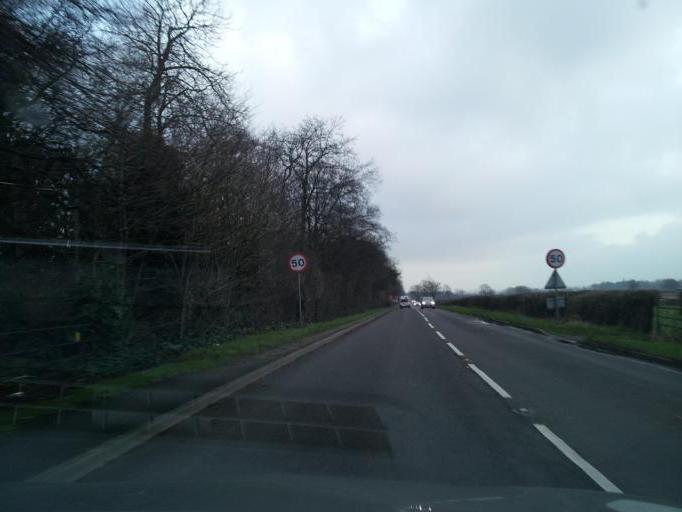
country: GB
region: England
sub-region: Derbyshire
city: Etwall
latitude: 52.8604
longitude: -1.6061
